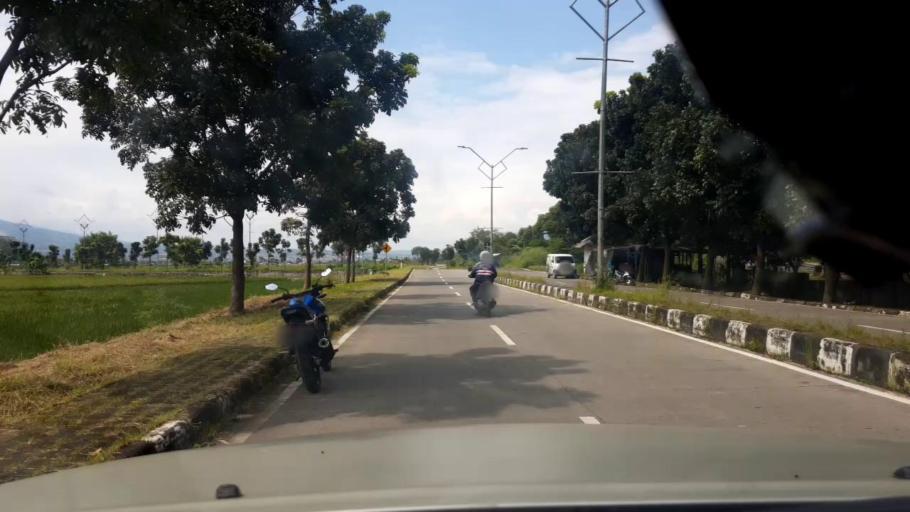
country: ID
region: West Java
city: Cileunyi
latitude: -6.9651
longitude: 107.7086
